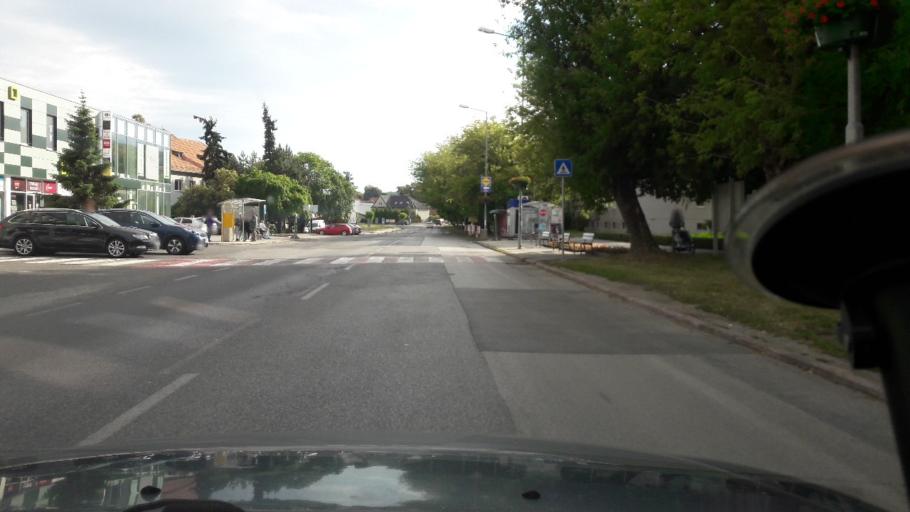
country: SK
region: Bratislavsky
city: Modra
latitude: 48.3345
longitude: 17.3072
